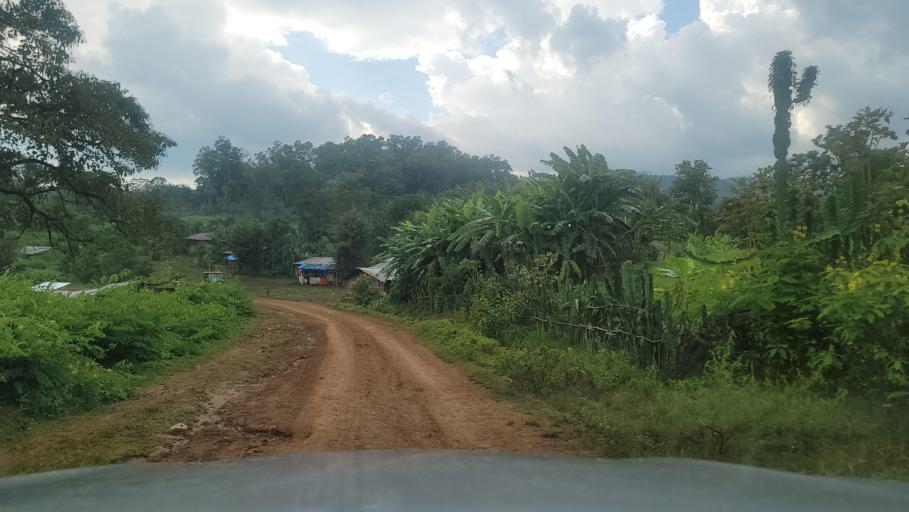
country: ET
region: Southern Nations, Nationalities, and People's Region
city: Bonga
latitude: 7.6338
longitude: 36.2223
